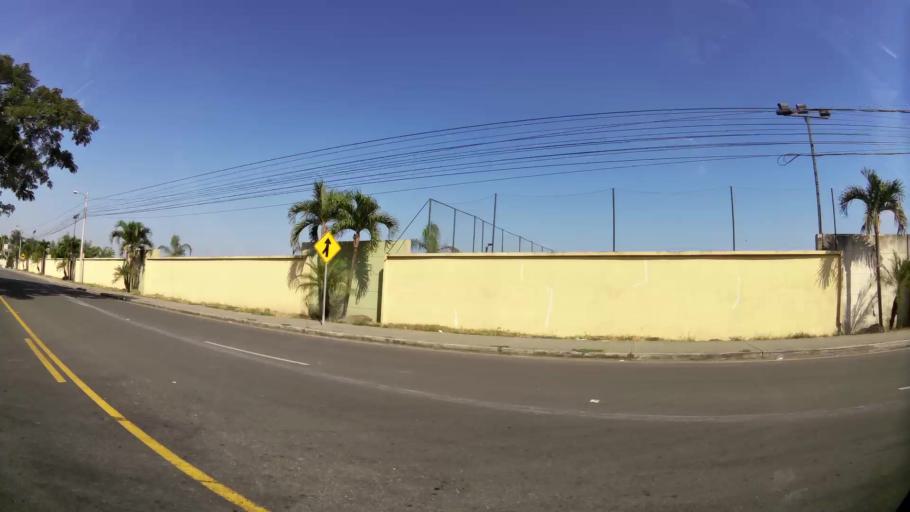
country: EC
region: Guayas
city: Santa Lucia
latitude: -2.1856
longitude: -80.0053
